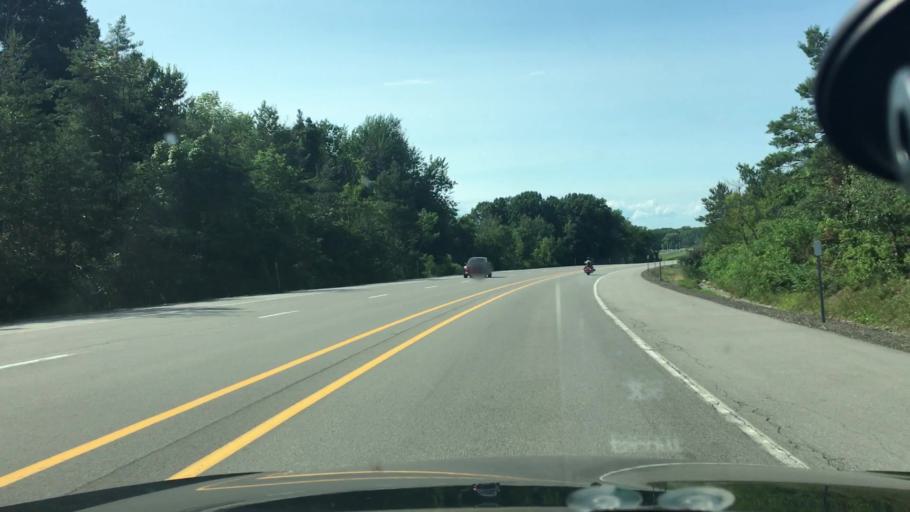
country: US
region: New York
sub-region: Chautauqua County
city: Silver Creek
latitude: 42.5542
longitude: -79.1119
